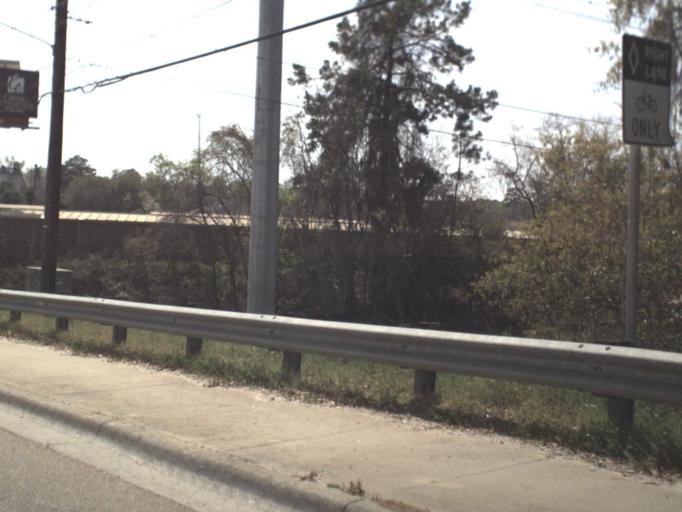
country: US
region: Florida
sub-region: Leon County
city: Tallahassee
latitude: 30.4580
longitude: -84.2278
